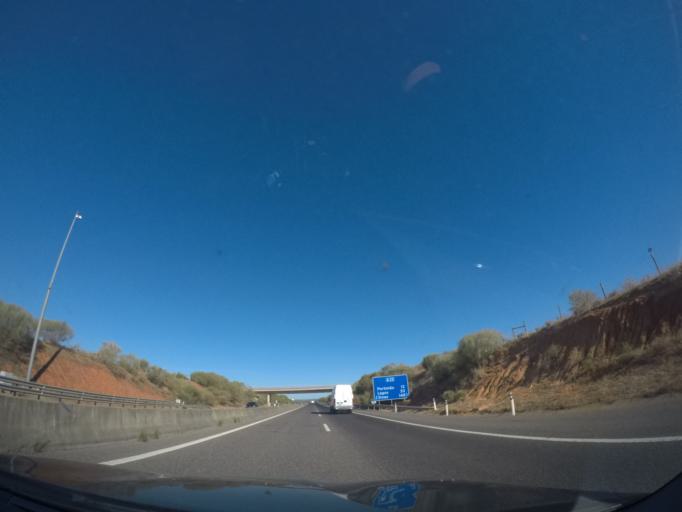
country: PT
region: Faro
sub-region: Lagoa
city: Lagoa
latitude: 37.1548
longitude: -8.4617
